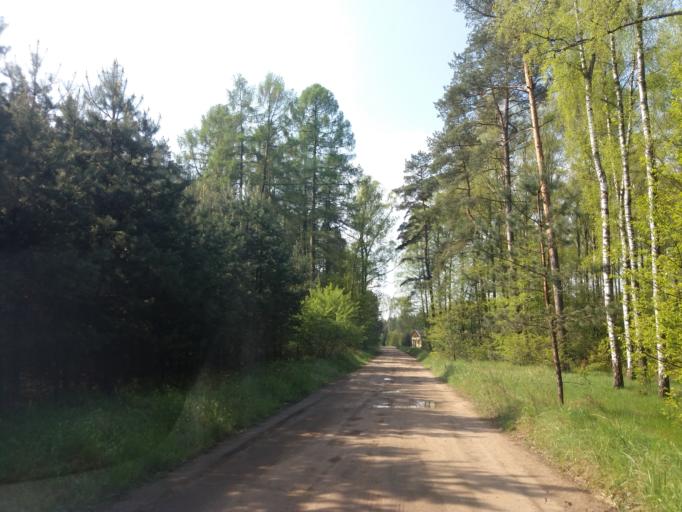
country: PL
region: West Pomeranian Voivodeship
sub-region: Powiat choszczenski
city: Drawno
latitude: 53.2319
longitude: 15.8194
